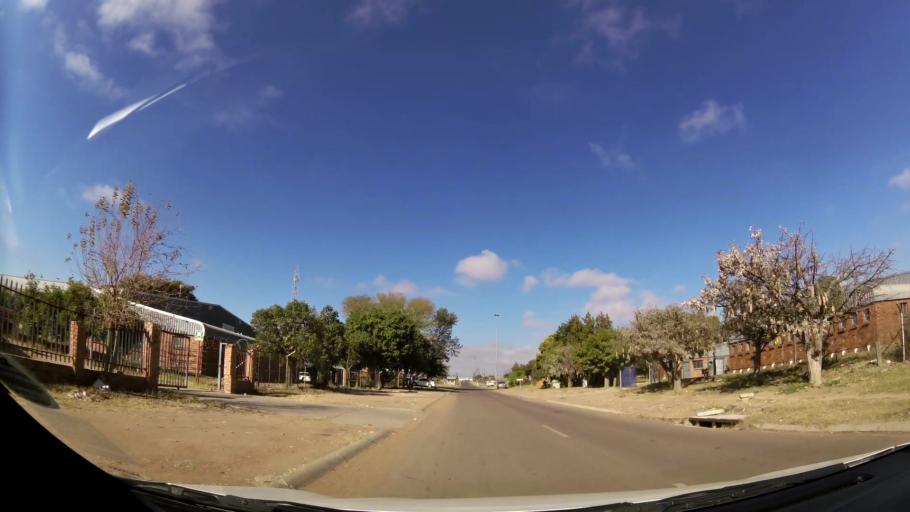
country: ZA
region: Limpopo
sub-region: Capricorn District Municipality
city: Polokwane
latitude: -23.8445
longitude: 29.4006
